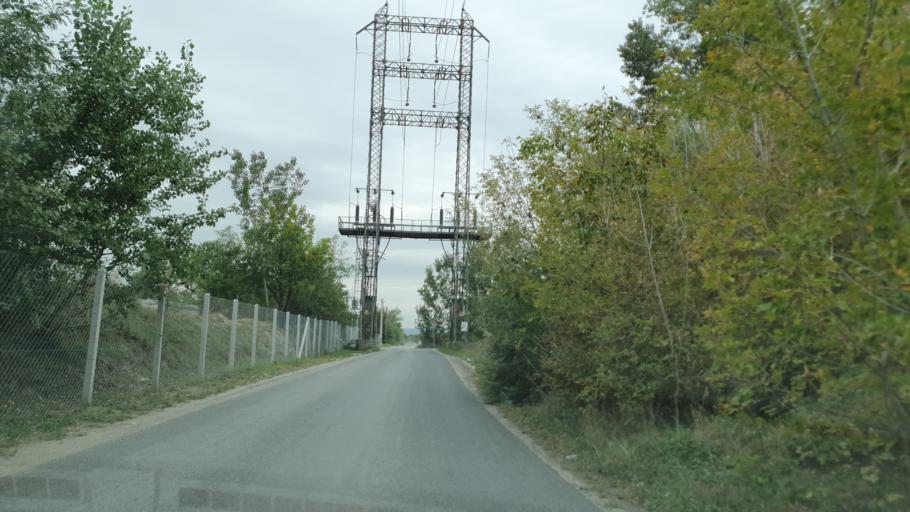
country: HU
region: Budapest
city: Budapest XXI. keruelet
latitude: 47.3981
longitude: 19.0636
